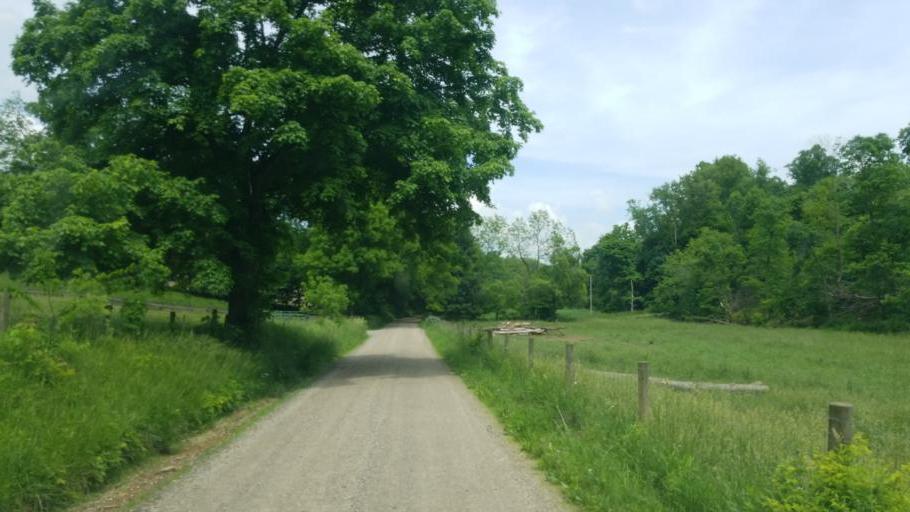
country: US
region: Ohio
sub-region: Coshocton County
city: West Lafayette
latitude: 40.4014
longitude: -81.7992
